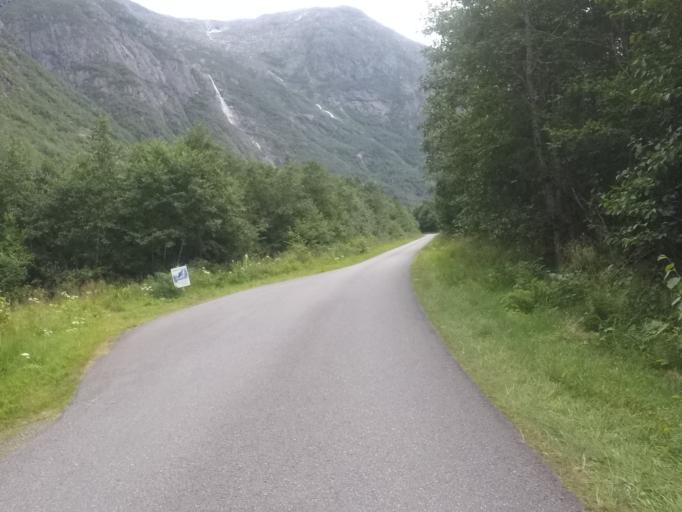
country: NO
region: Sogn og Fjordane
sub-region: Stryn
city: Stryn
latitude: 61.7747
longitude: 7.0220
